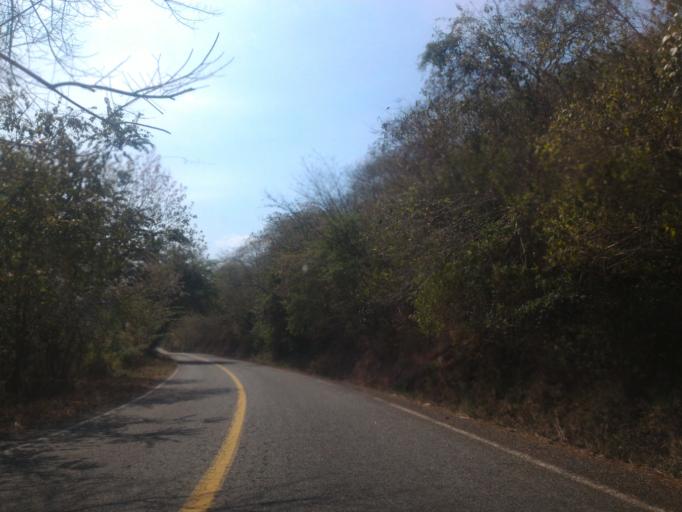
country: MX
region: Michoacan
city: Coahuayana Viejo
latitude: 18.3436
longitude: -103.4834
